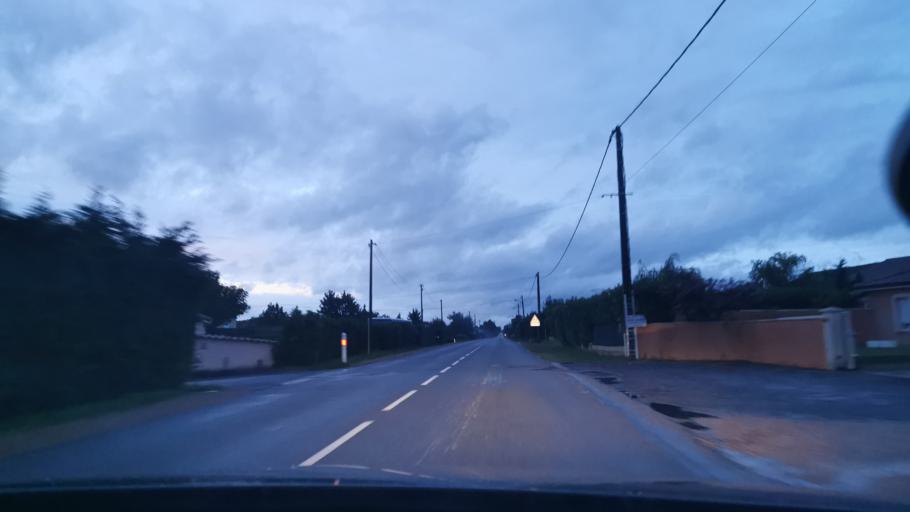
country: FR
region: Rhone-Alpes
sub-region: Departement de l'Ain
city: Bage-la-Ville
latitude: 46.3189
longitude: 4.9336
